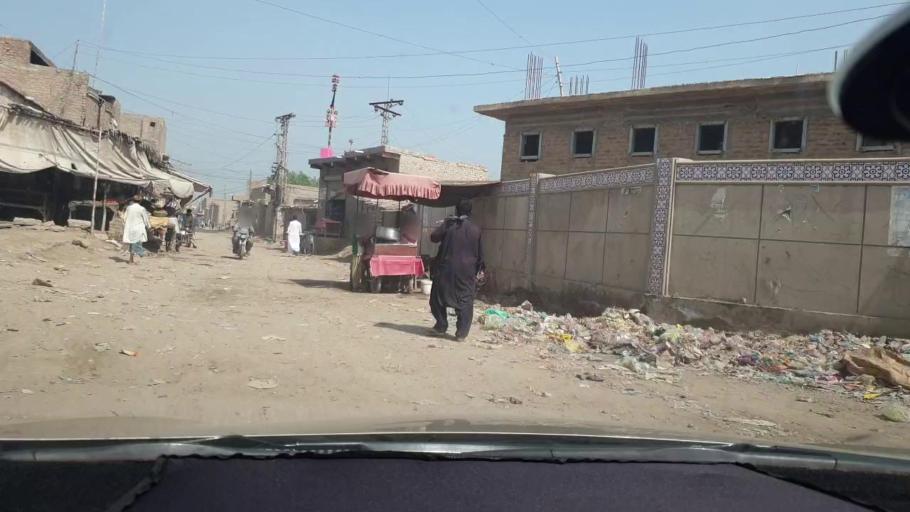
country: PK
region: Sindh
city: Kambar
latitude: 27.5825
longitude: 68.0040
